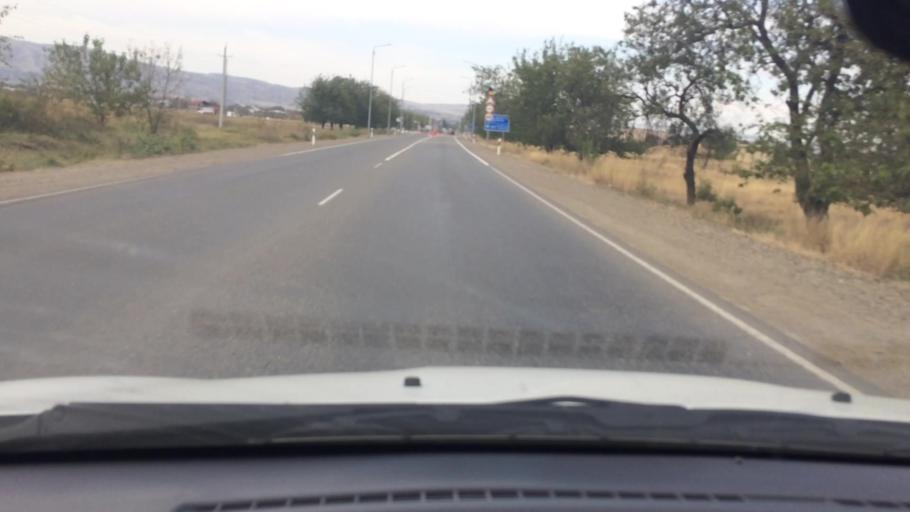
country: GE
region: Kvemo Kartli
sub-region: Marneuli
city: Marneuli
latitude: 41.5686
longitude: 44.7752
